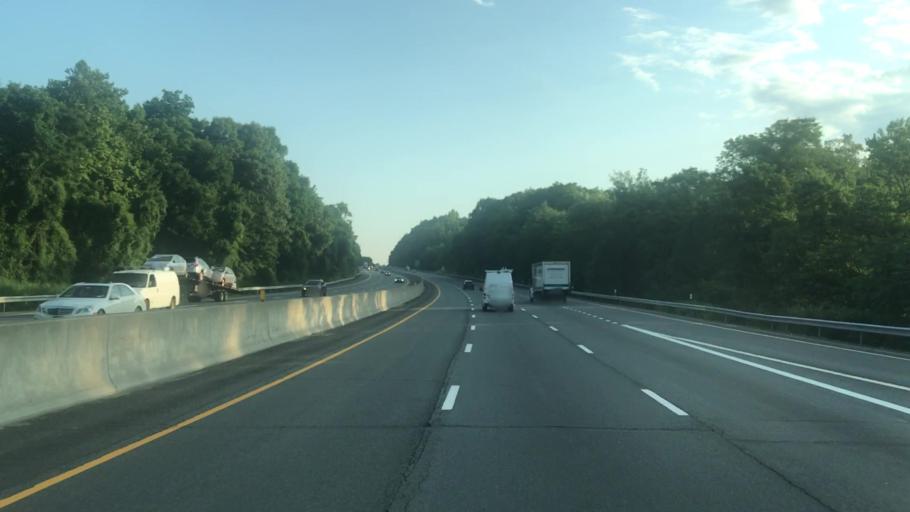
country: US
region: New York
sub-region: Westchester County
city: Ardsley
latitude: 40.9866
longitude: -73.8531
